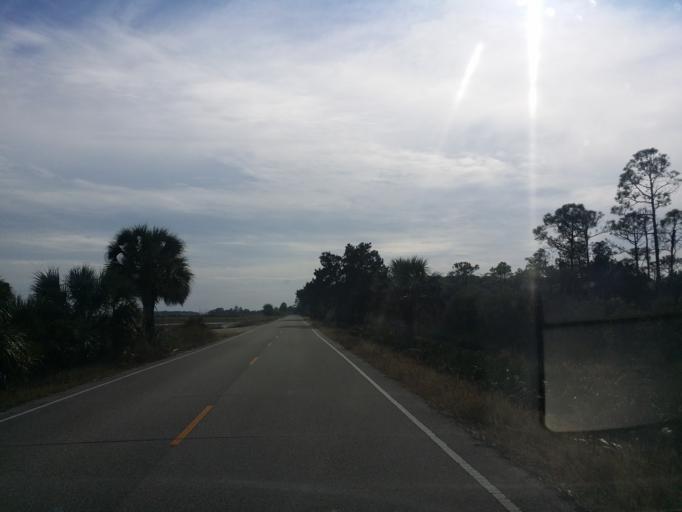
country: US
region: Florida
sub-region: Leon County
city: Woodville
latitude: 30.1169
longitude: -84.1486
